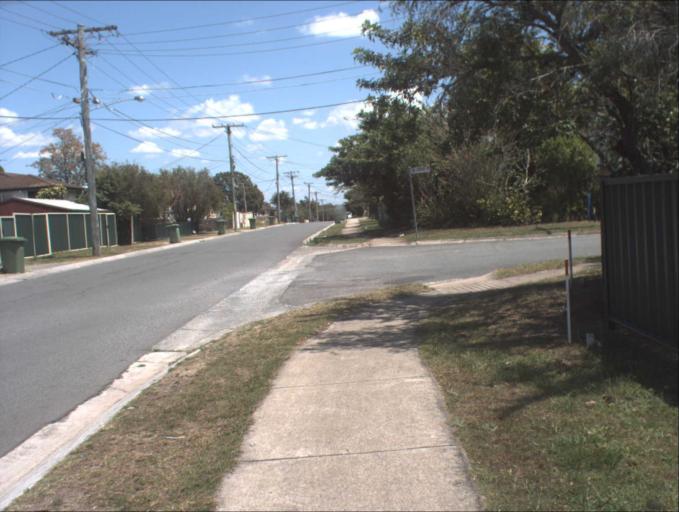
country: AU
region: Queensland
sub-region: Logan
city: Logan City
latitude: -27.6516
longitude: 153.1047
